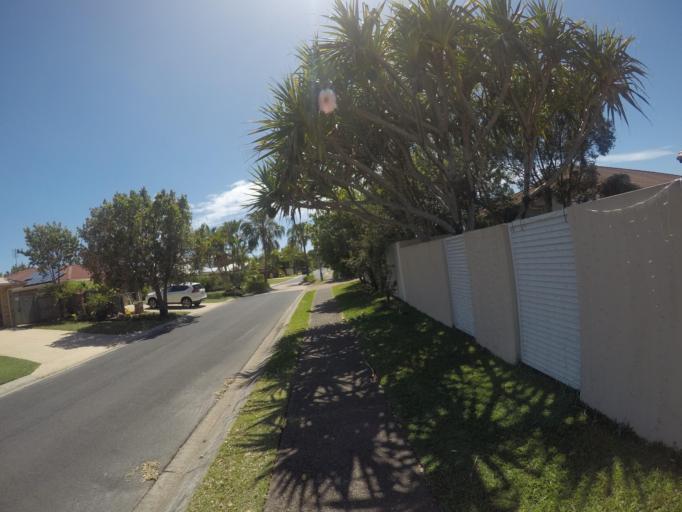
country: AU
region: Queensland
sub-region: Sunshine Coast
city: Mooloolaba
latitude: -26.6137
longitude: 153.0940
